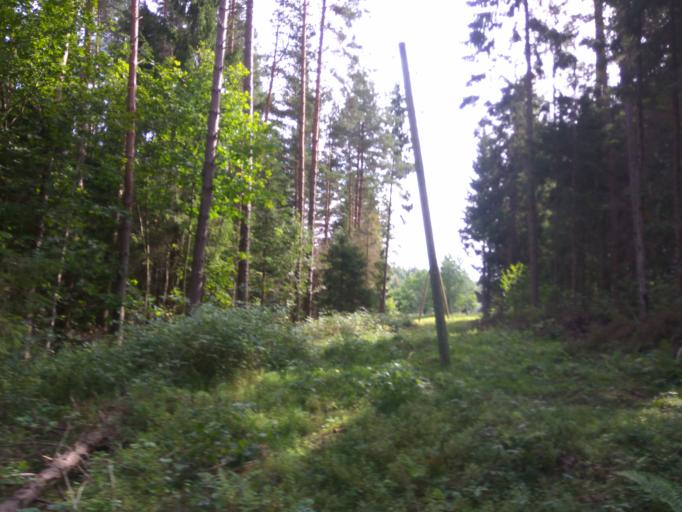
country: LV
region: Alsunga
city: Alsunga
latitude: 56.9853
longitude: 21.6773
